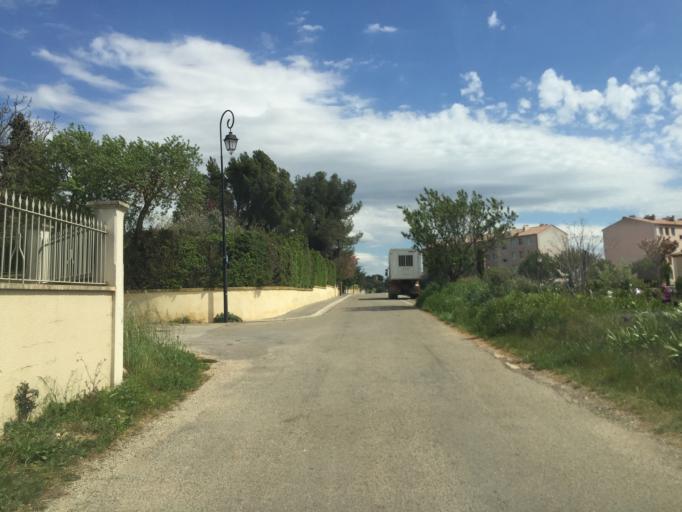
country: FR
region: Provence-Alpes-Cote d'Azur
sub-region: Departement du Vaucluse
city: Chateauneuf-du-Pape
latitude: 44.0541
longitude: 4.8211
